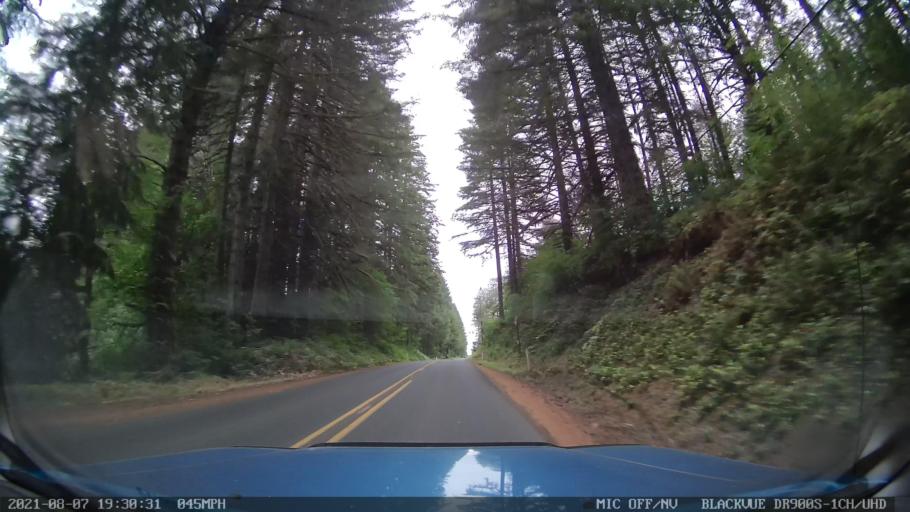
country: US
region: Oregon
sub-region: Linn County
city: Lyons
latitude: 44.8856
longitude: -122.6218
